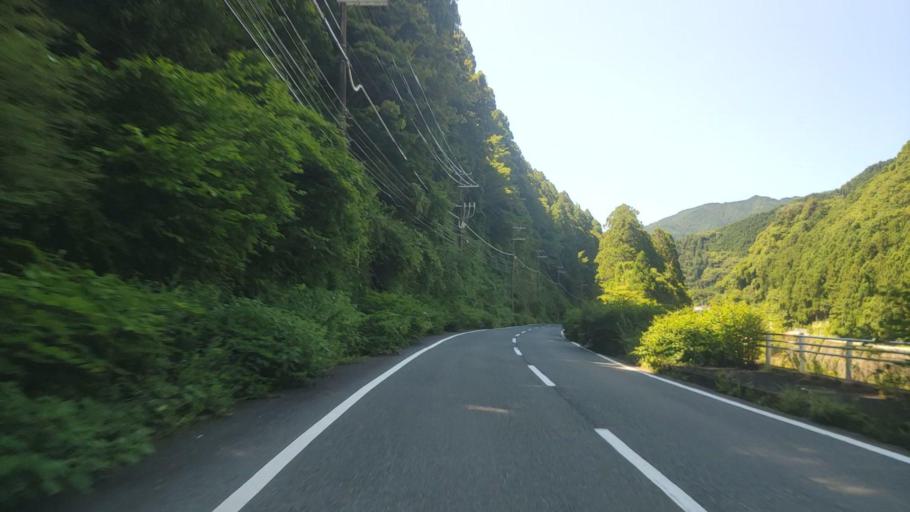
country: JP
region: Nara
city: Yoshino-cho
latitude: 34.2963
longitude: 136.0015
